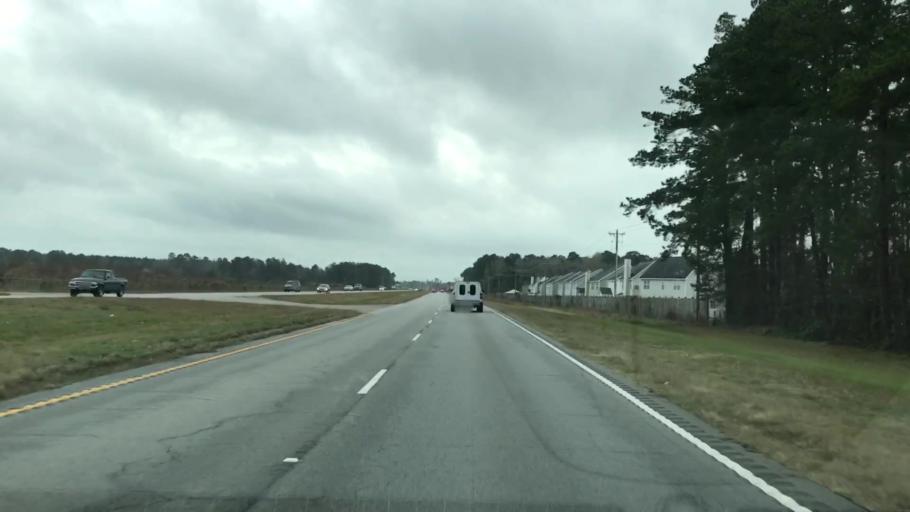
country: US
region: South Carolina
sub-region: Berkeley County
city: Moncks Corner
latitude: 33.1544
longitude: -80.0330
